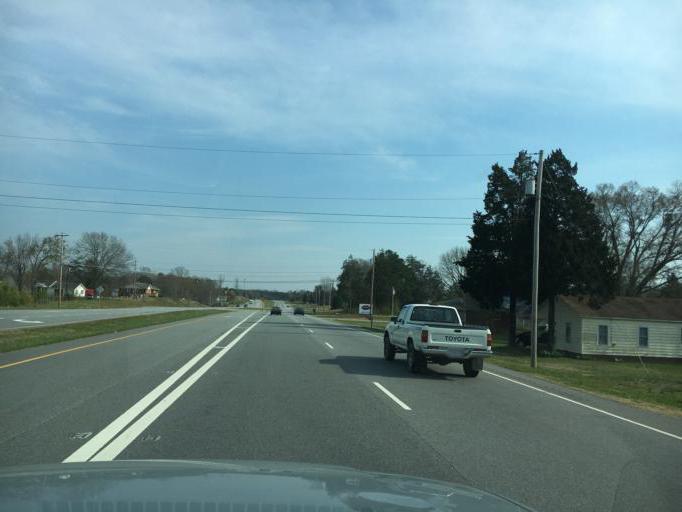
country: US
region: North Carolina
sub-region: Rutherford County
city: Forest City
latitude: 35.2881
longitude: -81.9049
